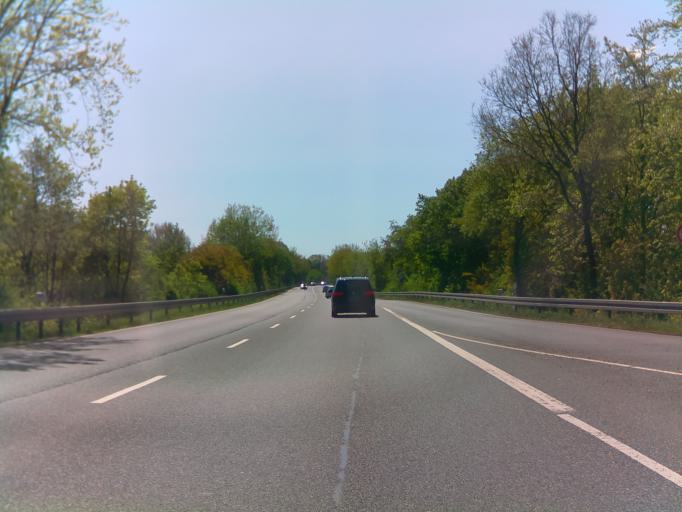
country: DE
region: Hesse
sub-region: Regierungsbezirk Kassel
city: Bad Hersfeld
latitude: 50.8598
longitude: 9.7082
